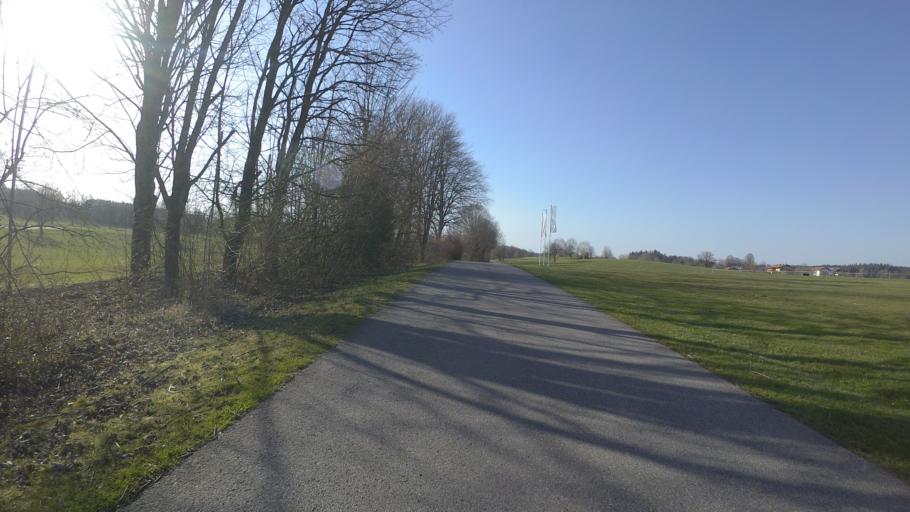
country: DE
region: Bavaria
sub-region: Upper Bavaria
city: Traunreut
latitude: 47.9345
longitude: 12.5580
